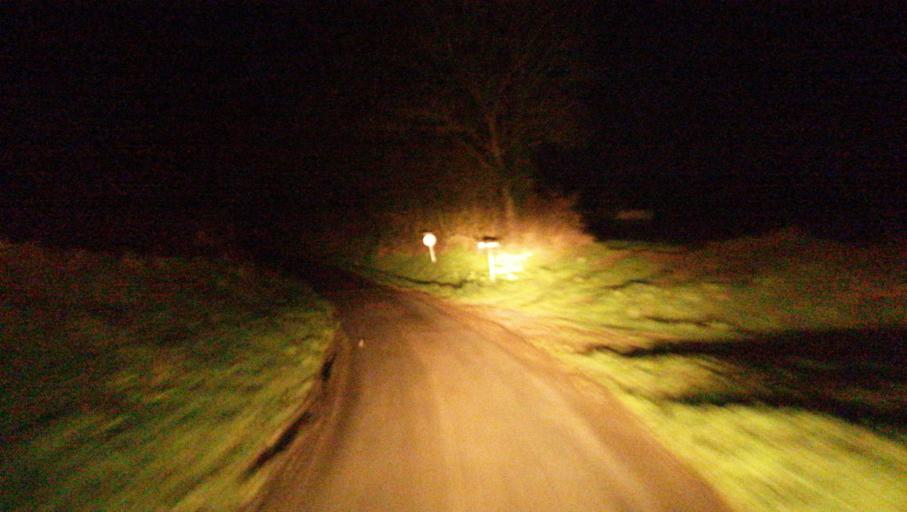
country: FR
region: Brittany
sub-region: Departement des Cotes-d'Armor
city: Plehedel
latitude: 48.6790
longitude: -3.0312
